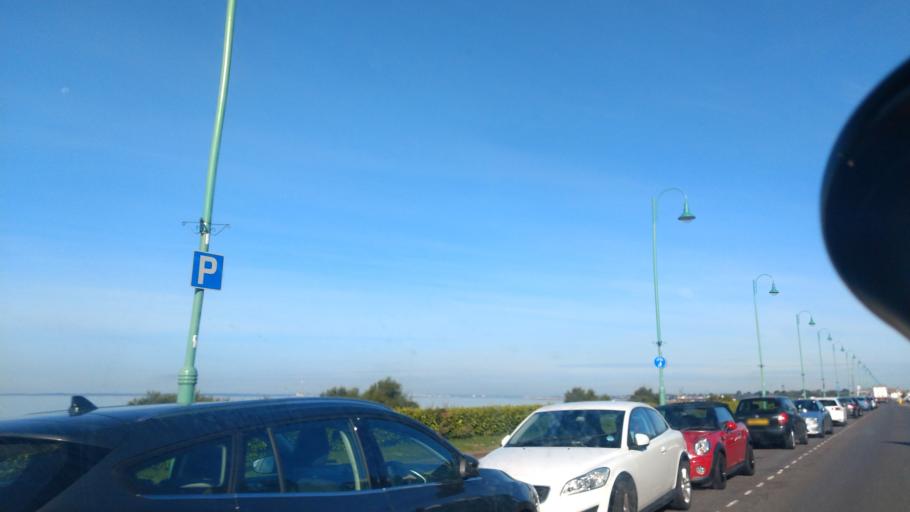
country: GB
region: England
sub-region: Hampshire
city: Lee-on-the-Solent
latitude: 50.8027
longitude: -1.2046
